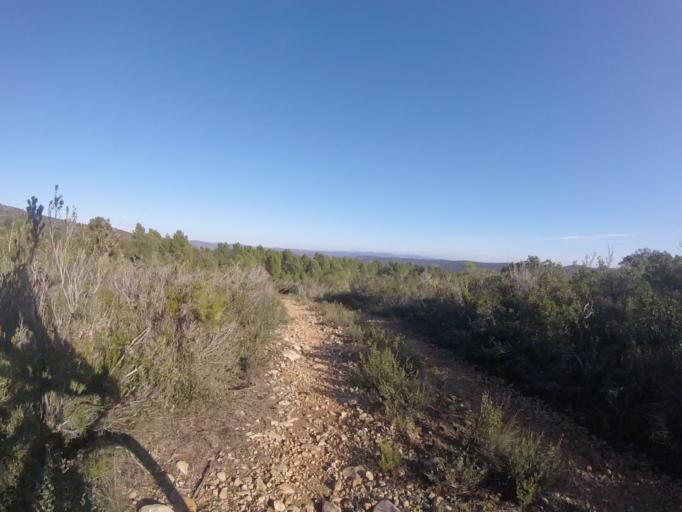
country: ES
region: Valencia
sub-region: Provincia de Castello
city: Sarratella
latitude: 40.2857
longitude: 0.0623
